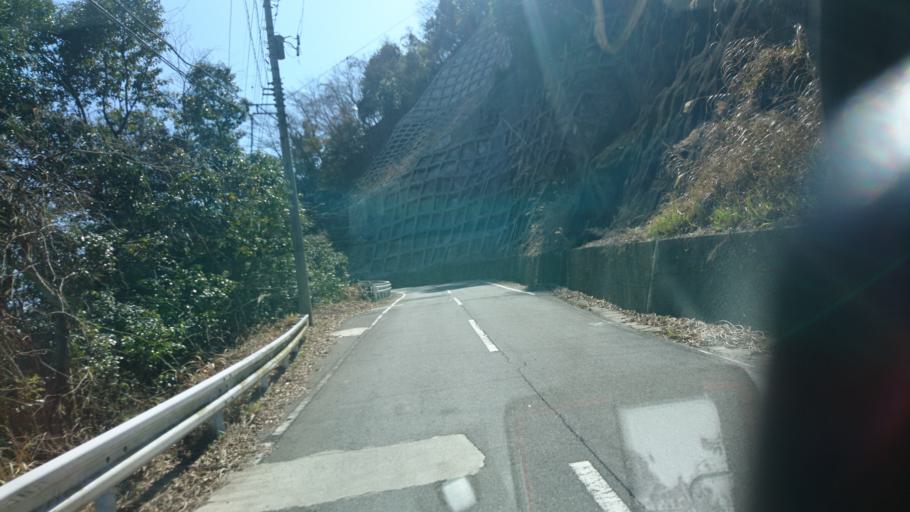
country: JP
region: Shizuoka
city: Fujinomiya
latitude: 35.3550
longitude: 138.4381
